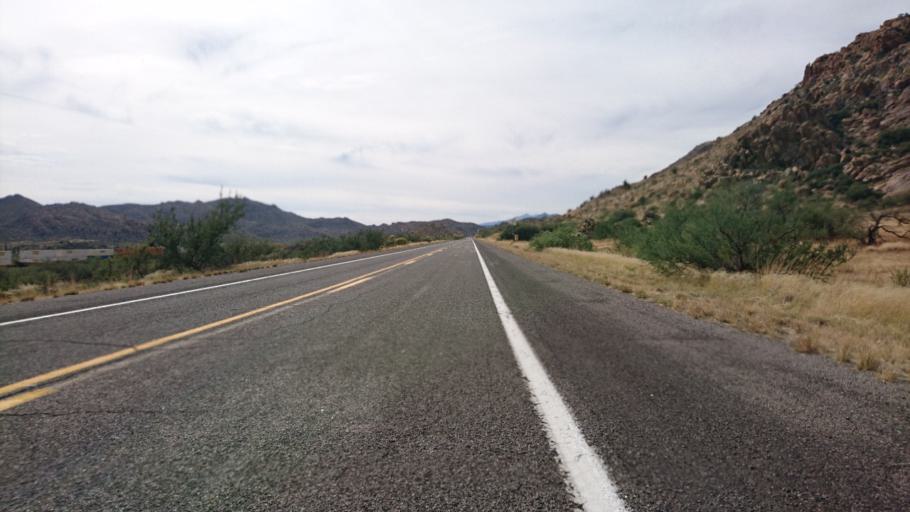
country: US
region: Arizona
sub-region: Mohave County
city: Peach Springs
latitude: 35.3811
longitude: -113.6638
